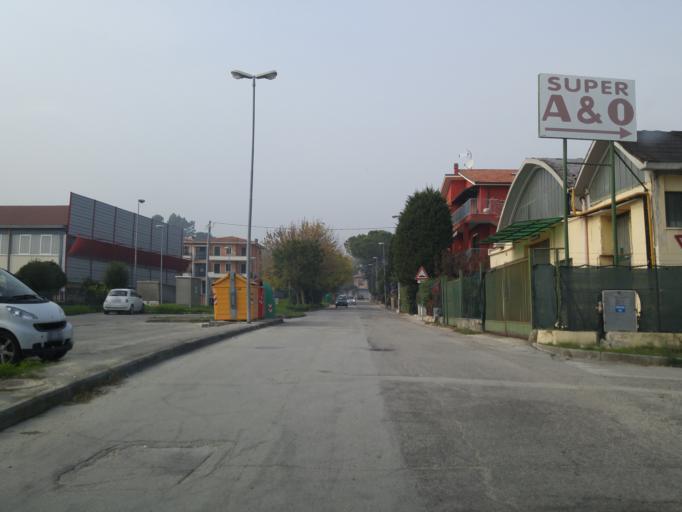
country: IT
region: The Marches
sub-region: Provincia di Pesaro e Urbino
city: Calcinelli
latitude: 43.7521
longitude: 12.9230
